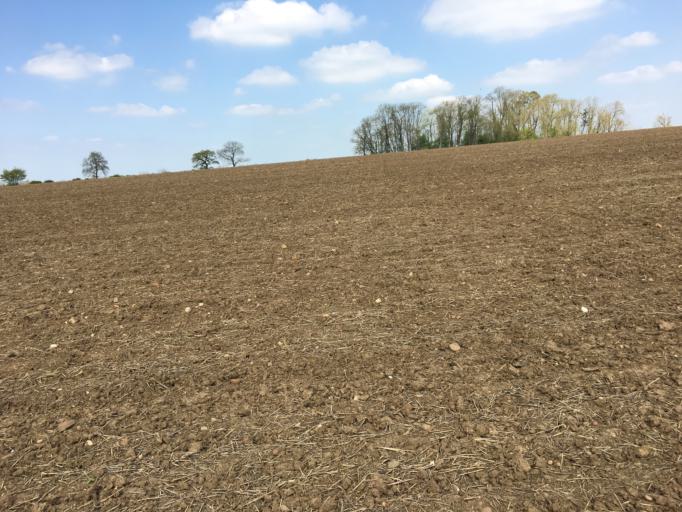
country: GB
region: England
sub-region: Leicestershire
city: Houghton on the Hill
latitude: 52.6077
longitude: -0.9948
